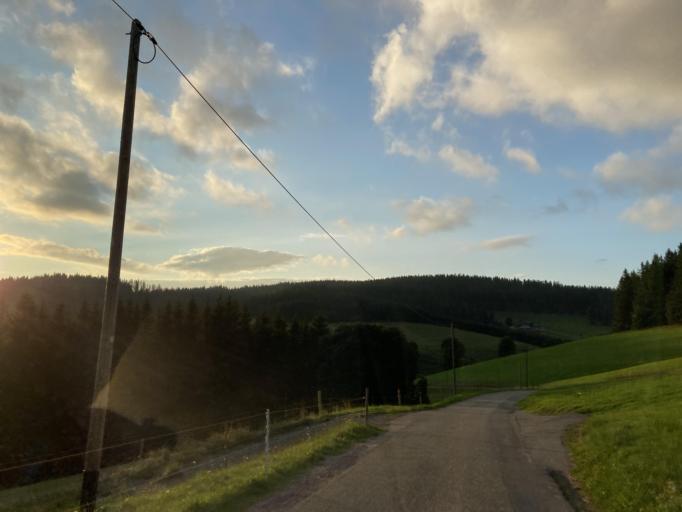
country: DE
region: Baden-Wuerttemberg
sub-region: Freiburg Region
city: Vohrenbach
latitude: 48.0805
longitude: 8.2768
